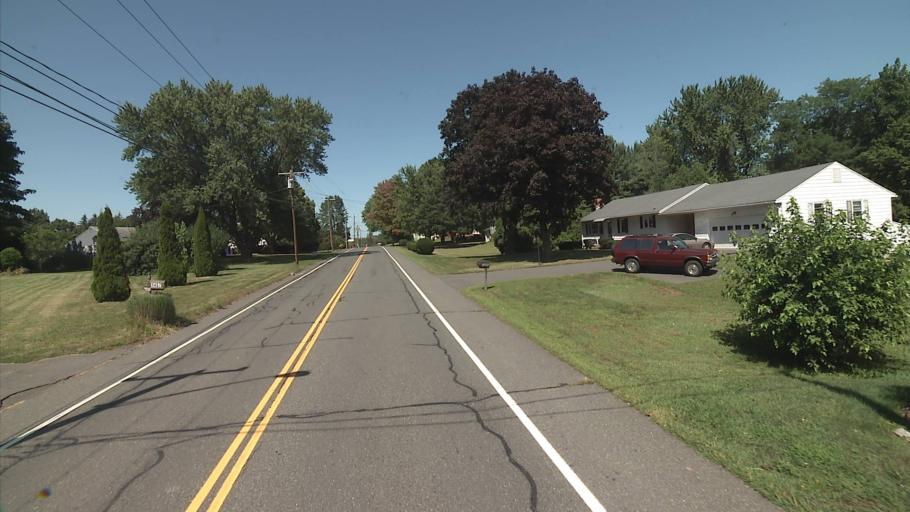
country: US
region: Connecticut
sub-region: Hartford County
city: Thompsonville
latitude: 42.0173
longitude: -72.6167
